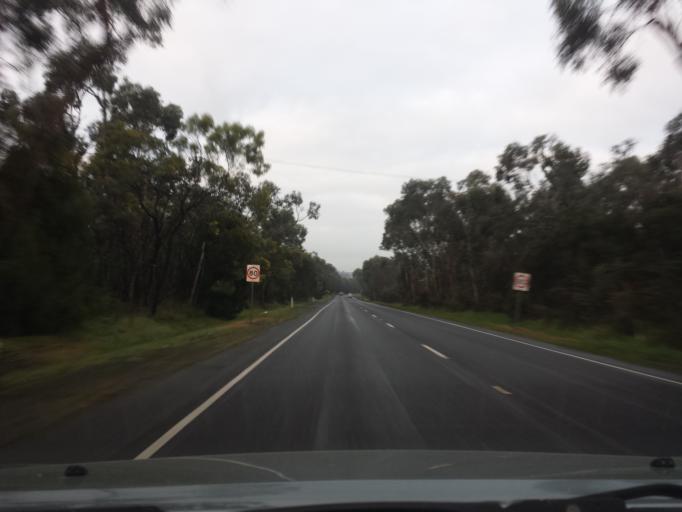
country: AU
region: Victoria
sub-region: Yarra Ranges
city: Belgrave South
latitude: -37.9587
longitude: 145.3455
